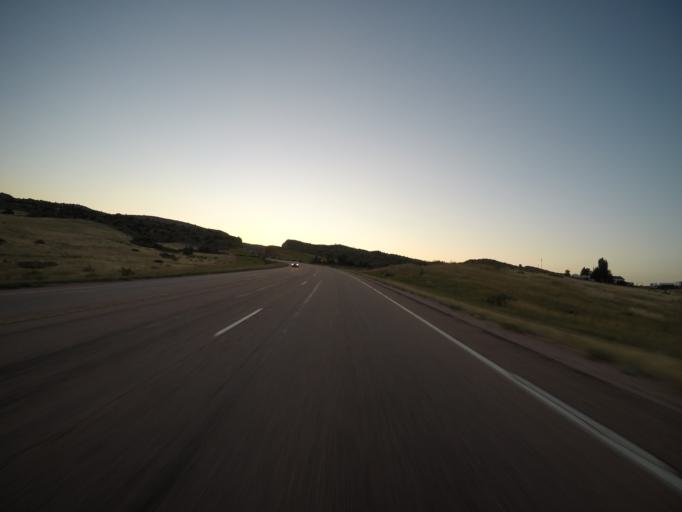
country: US
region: Colorado
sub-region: Larimer County
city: Laporte
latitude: 40.7600
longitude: -105.1737
